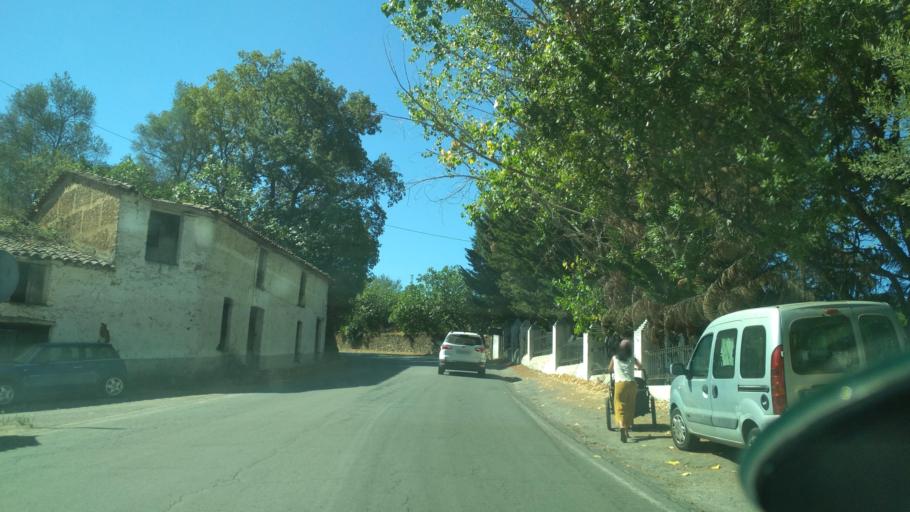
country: ES
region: Andalusia
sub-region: Provincia de Huelva
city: Galaroza
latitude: 37.9234
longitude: -6.7068
